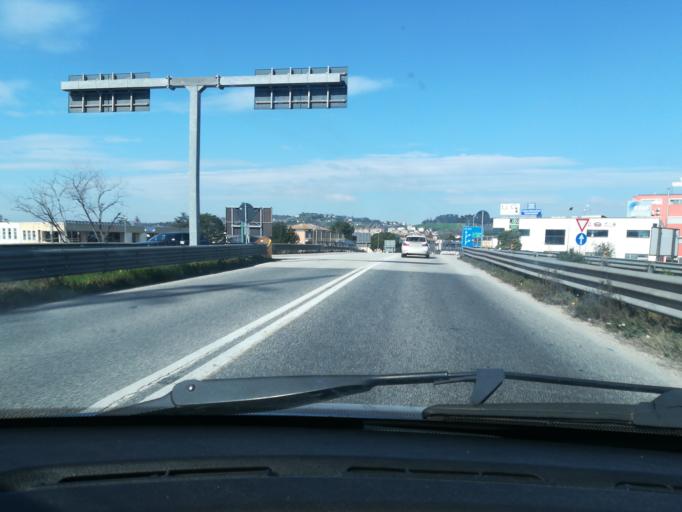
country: IT
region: The Marches
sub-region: Provincia di Macerata
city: Santa Maria Apparente
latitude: 43.2890
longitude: 13.7088
